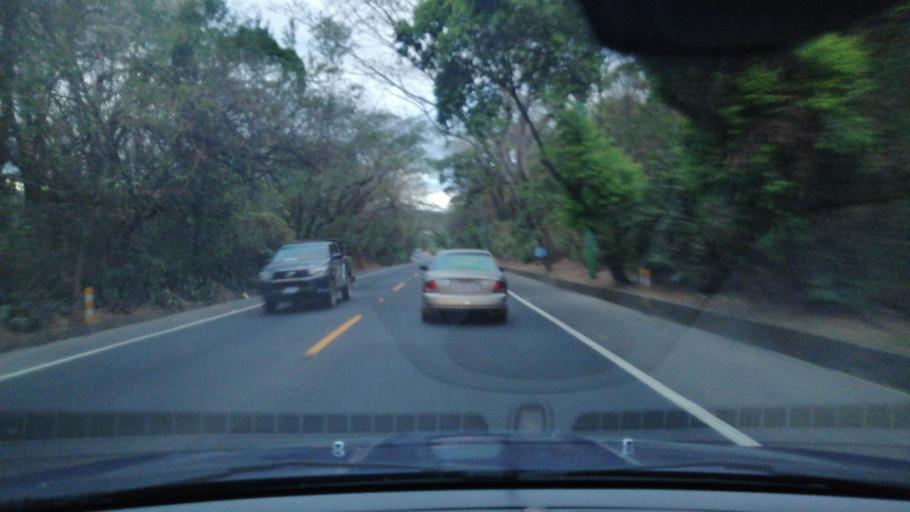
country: SV
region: Santa Ana
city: Santa Ana
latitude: 13.9950
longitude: -89.5415
